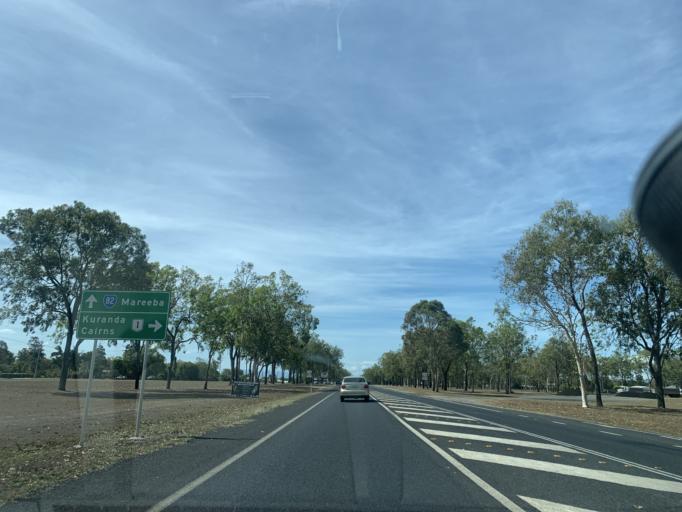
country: AU
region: Queensland
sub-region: Tablelands
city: Mareeba
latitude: -17.0171
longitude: 145.4257
